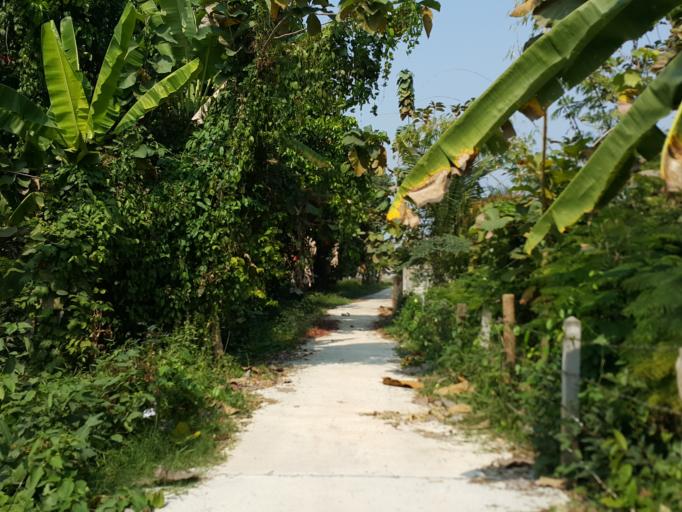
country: TH
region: Sukhothai
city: Thung Saliam
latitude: 17.3243
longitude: 99.5130
